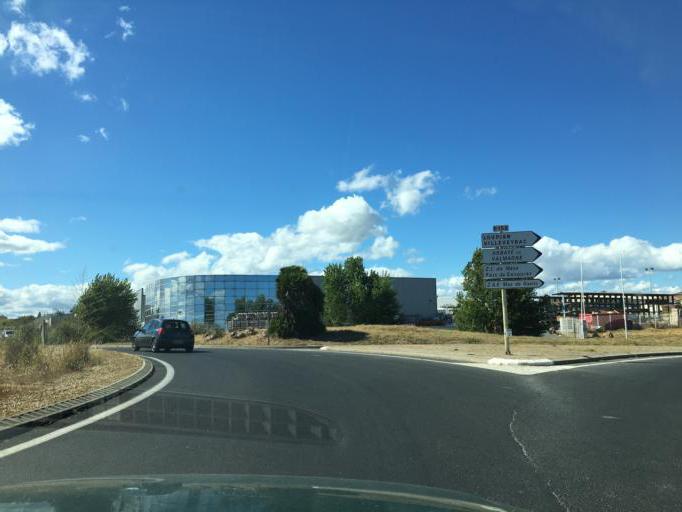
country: FR
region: Languedoc-Roussillon
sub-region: Departement de l'Herault
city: Meze
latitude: 43.4400
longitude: 3.5775
